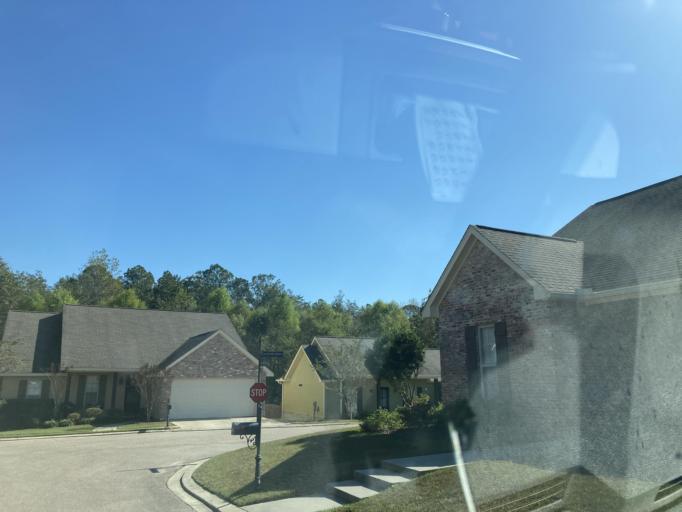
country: US
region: Mississippi
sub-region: Lamar County
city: West Hattiesburg
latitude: 31.3141
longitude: -89.4837
